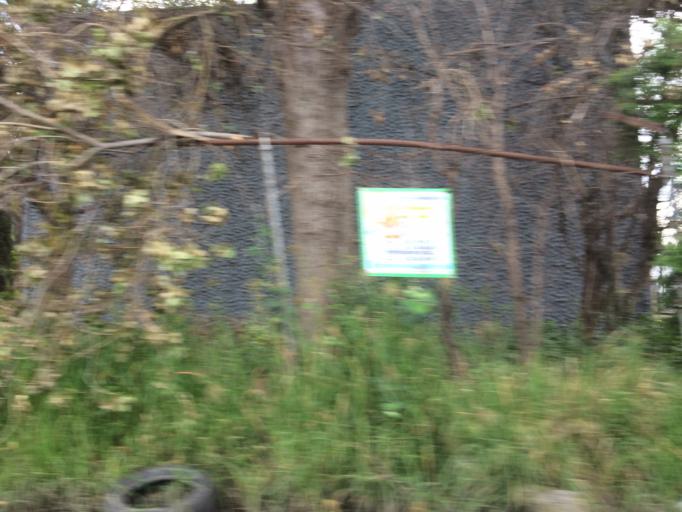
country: MX
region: Michoacan
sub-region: Morelia
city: Morelos
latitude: 19.6858
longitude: -101.2347
